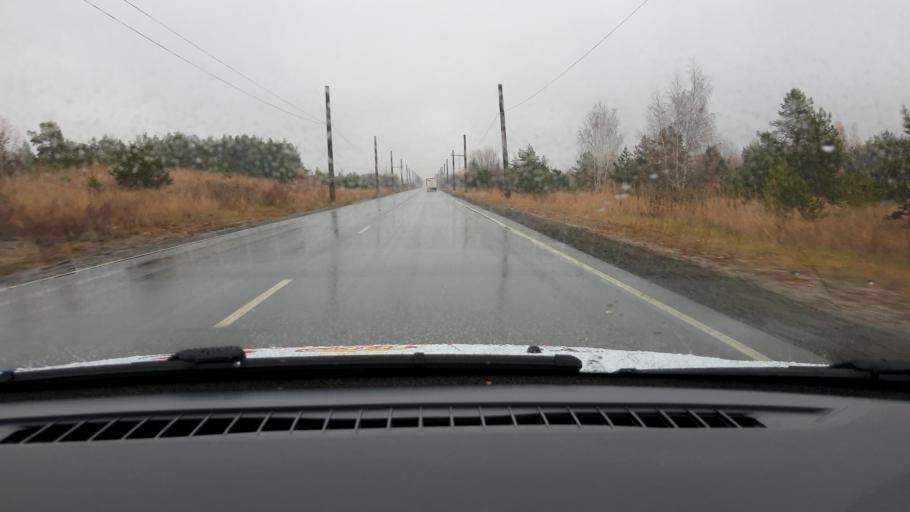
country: RU
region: Nizjnij Novgorod
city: Dzerzhinsk
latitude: 56.2626
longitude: 43.5224
